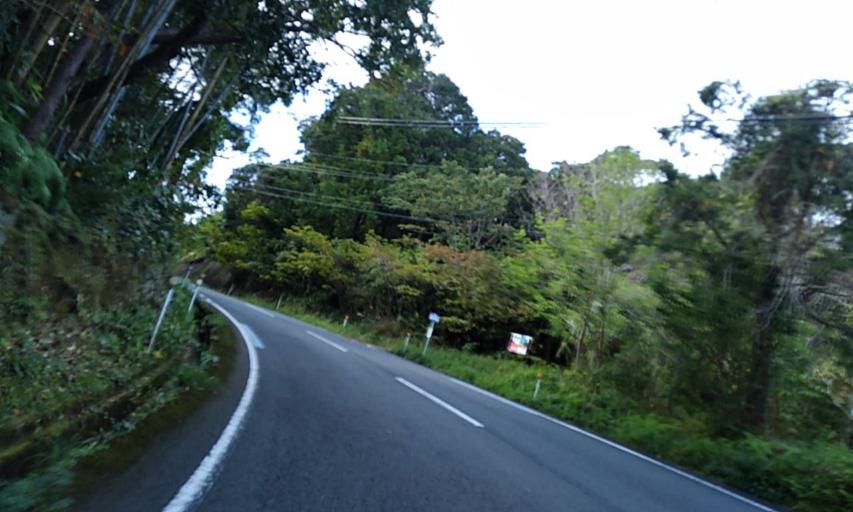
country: JP
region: Wakayama
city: Shingu
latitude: 33.4698
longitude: 135.8226
